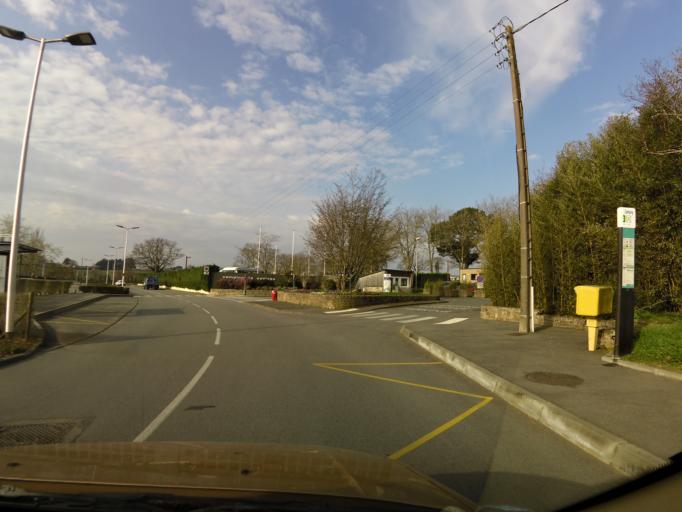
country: FR
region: Brittany
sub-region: Departement du Morbihan
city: Arradon
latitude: 47.6331
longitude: -2.7794
